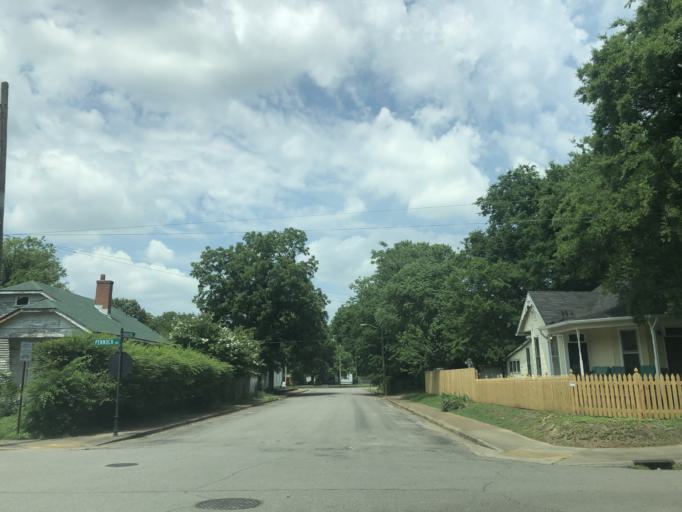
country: US
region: Tennessee
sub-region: Davidson County
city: Nashville
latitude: 36.1901
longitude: -86.7663
